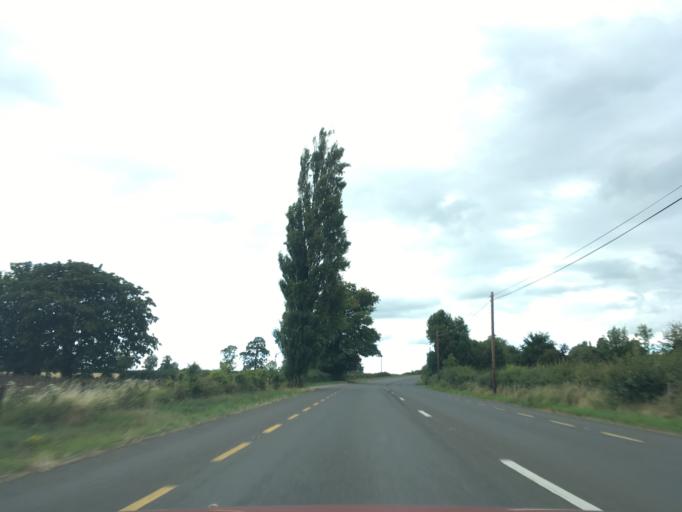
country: IE
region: Munster
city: Cahir
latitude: 52.4074
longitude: -7.8958
